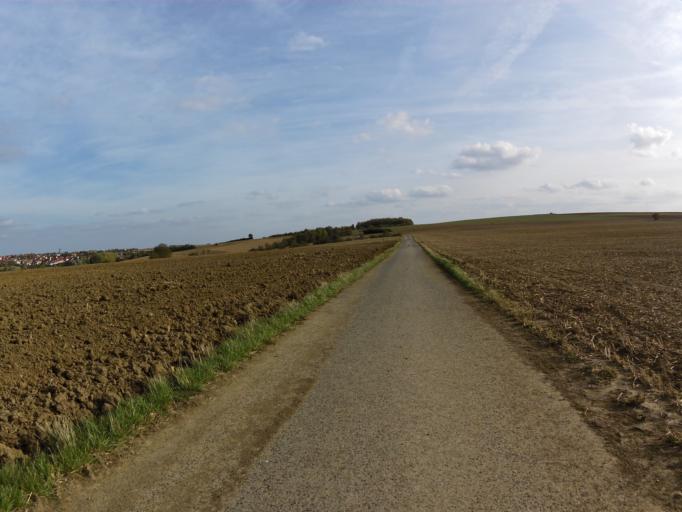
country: DE
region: Bavaria
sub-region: Regierungsbezirk Unterfranken
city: Reichenberg
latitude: 49.7264
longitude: 9.9456
